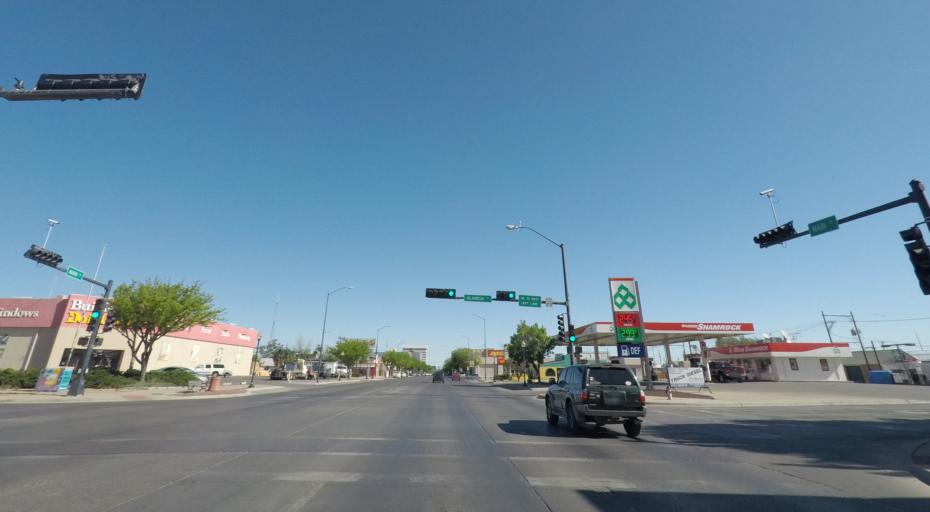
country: US
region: New Mexico
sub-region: Chaves County
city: Roswell
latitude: 33.3908
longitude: -104.5227
